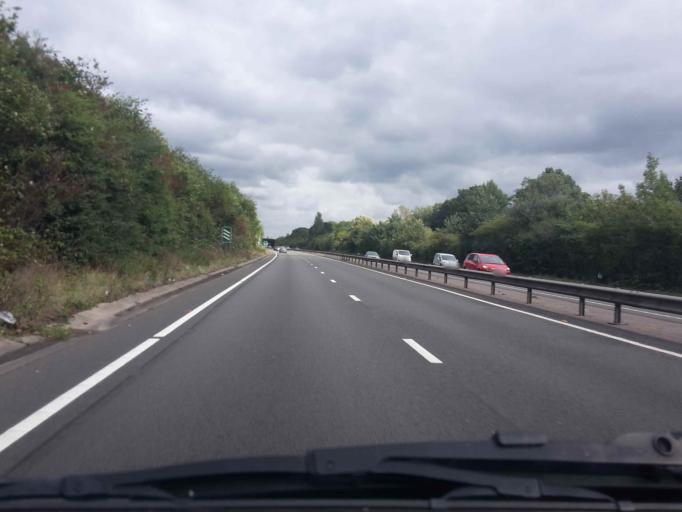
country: GB
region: England
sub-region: Hampshire
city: Farnborough
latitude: 51.2693
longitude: -0.7346
